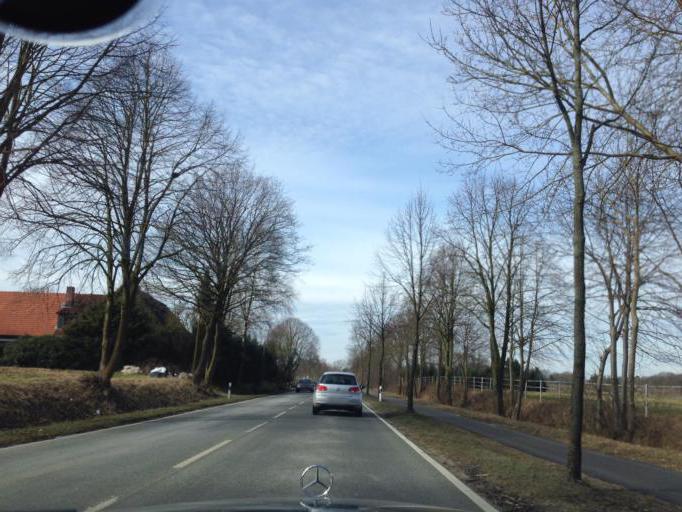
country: DE
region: Lower Saxony
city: Seevetal
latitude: 53.4388
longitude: 9.9113
